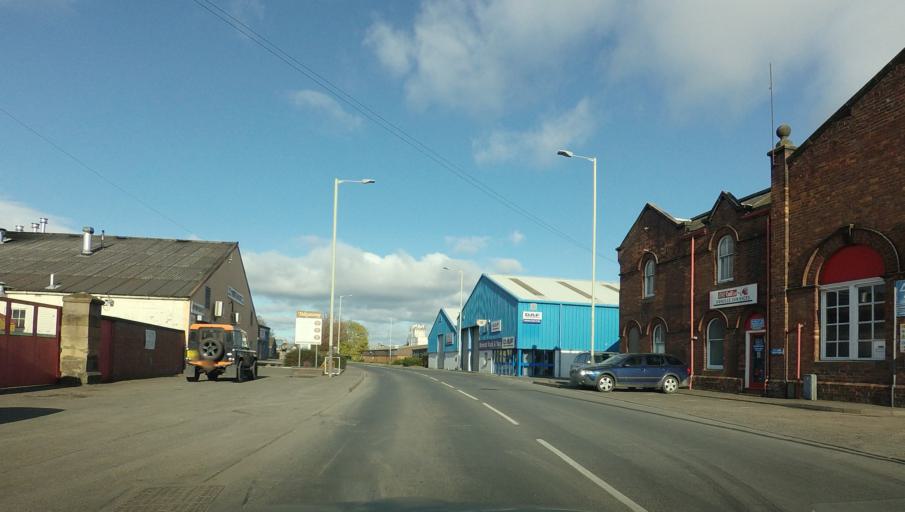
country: GB
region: Scotland
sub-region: Perth and Kinross
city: Perth
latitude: 56.3843
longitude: -3.4270
